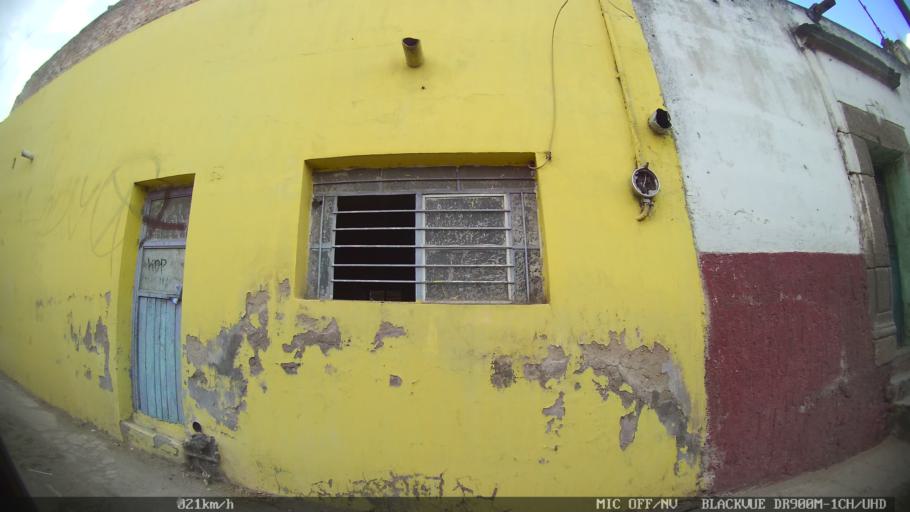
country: MX
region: Jalisco
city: Tlaquepaque
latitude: 20.6589
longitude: -103.2607
